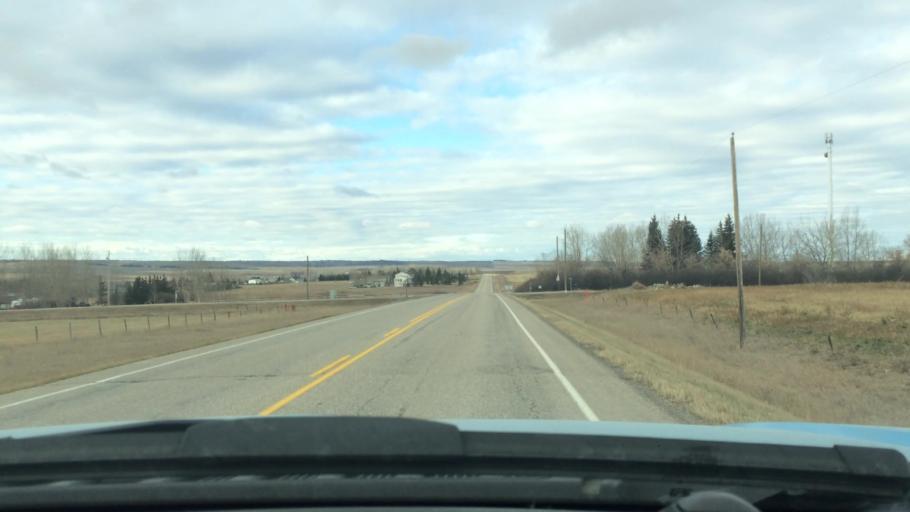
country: CA
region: Alberta
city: Airdrie
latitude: 51.2123
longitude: -114.1390
